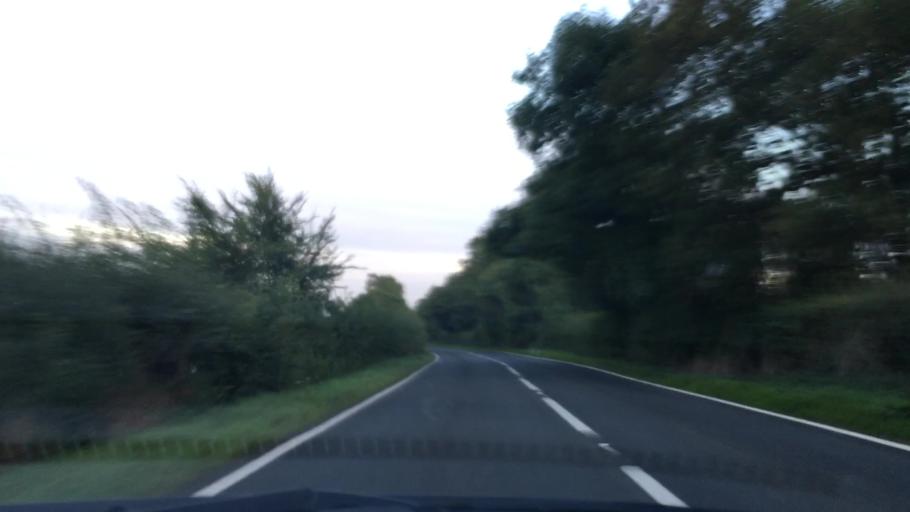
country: GB
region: England
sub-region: North East Lincolnshire
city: Wold Newton
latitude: 53.4637
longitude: -0.0997
